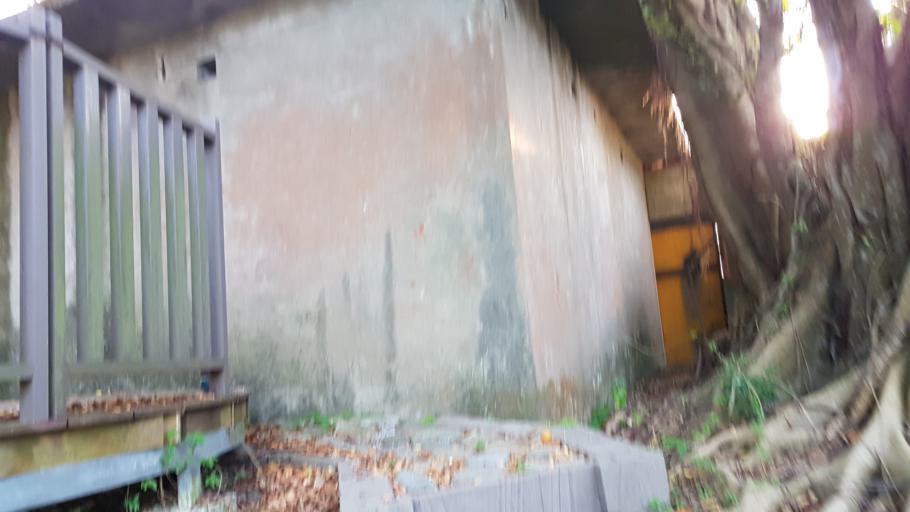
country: TW
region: Taipei
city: Taipei
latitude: 25.0214
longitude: 121.5615
